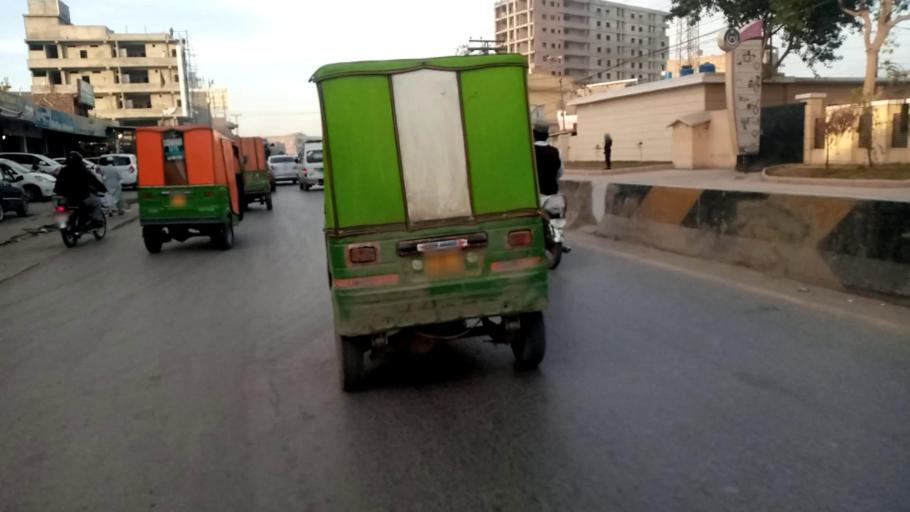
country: PK
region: Khyber Pakhtunkhwa
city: Peshawar
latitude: 34.0277
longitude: 71.5753
